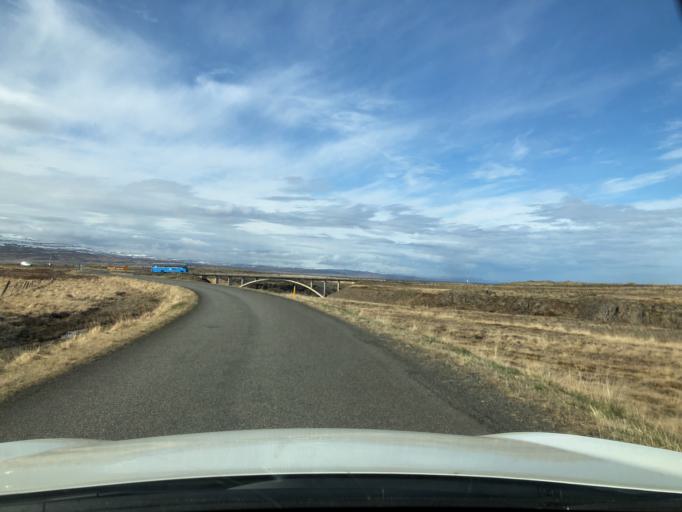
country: IS
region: West
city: Borgarnes
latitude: 65.0522
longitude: -21.6951
